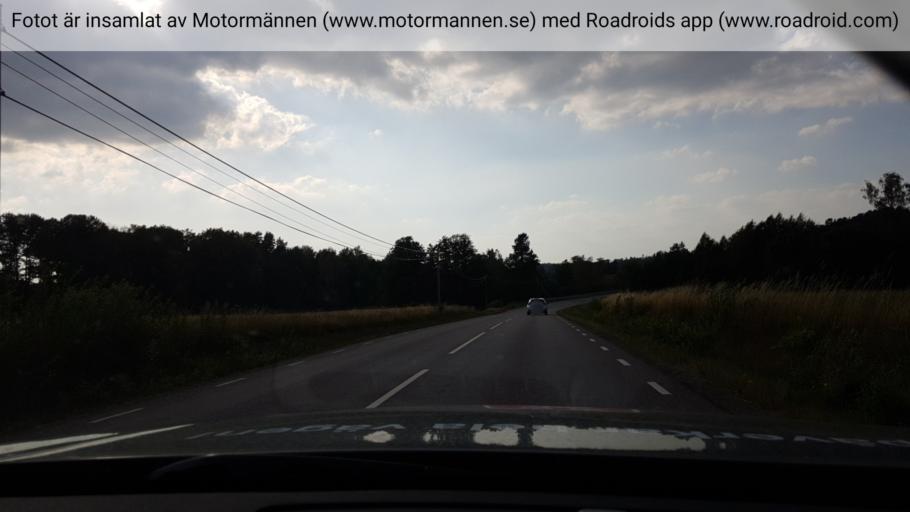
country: SE
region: Soedermanland
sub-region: Gnesta Kommun
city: Gnesta
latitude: 59.0719
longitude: 17.2902
